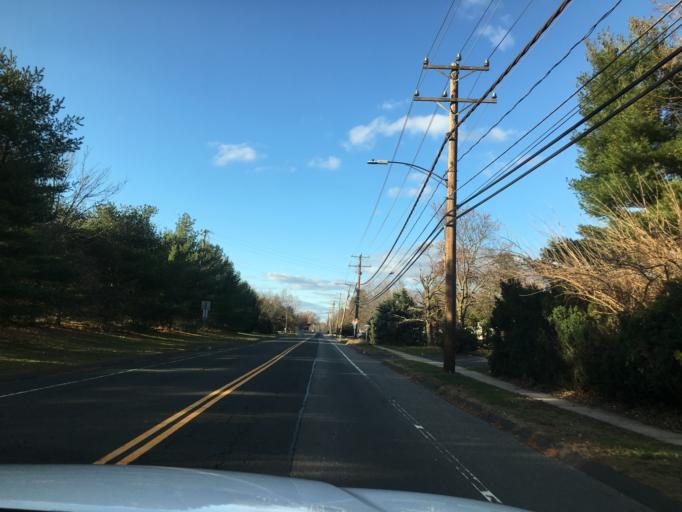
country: US
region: Connecticut
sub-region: Hartford County
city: Windsor Locks
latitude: 41.9150
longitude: -72.6601
